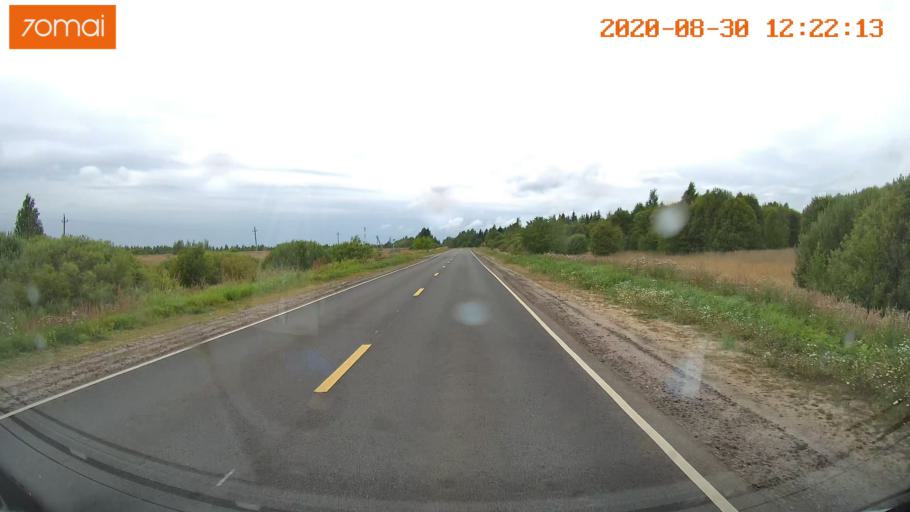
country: RU
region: Ivanovo
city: Yur'yevets
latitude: 57.3289
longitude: 42.8557
